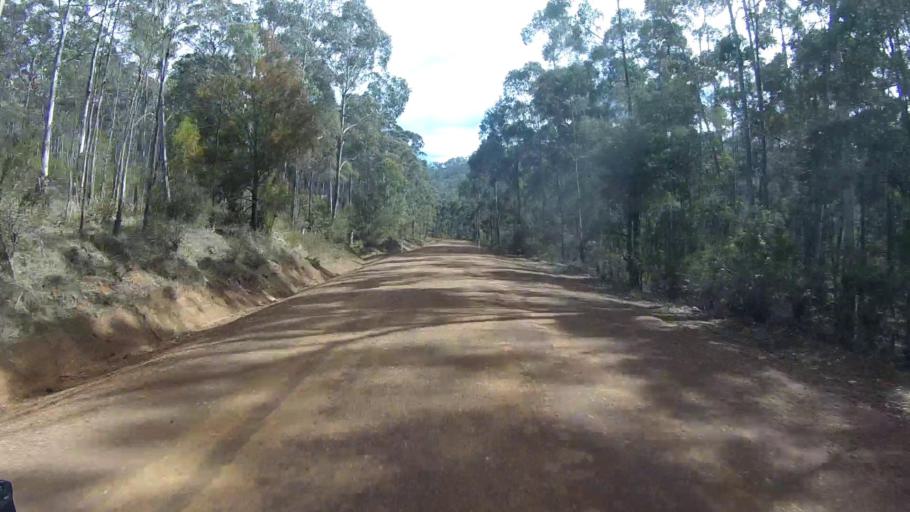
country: AU
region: Tasmania
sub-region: Sorell
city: Sorell
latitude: -42.6248
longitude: 147.9027
